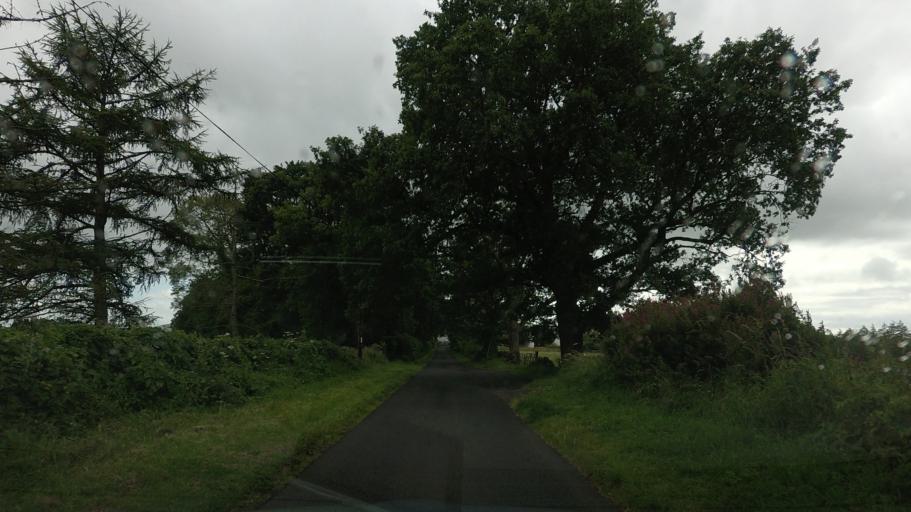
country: GB
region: Scotland
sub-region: Stirling
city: Killearn
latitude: 56.0716
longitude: -4.4508
